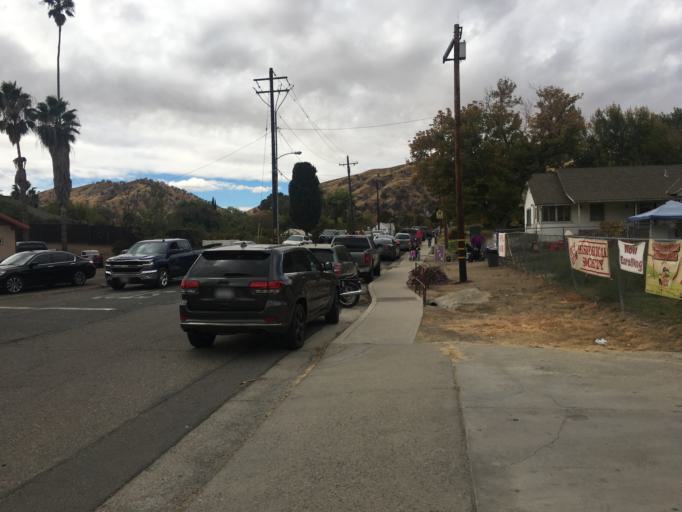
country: US
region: California
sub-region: Tulare County
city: East Porterville
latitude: 36.1294
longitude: -118.8197
